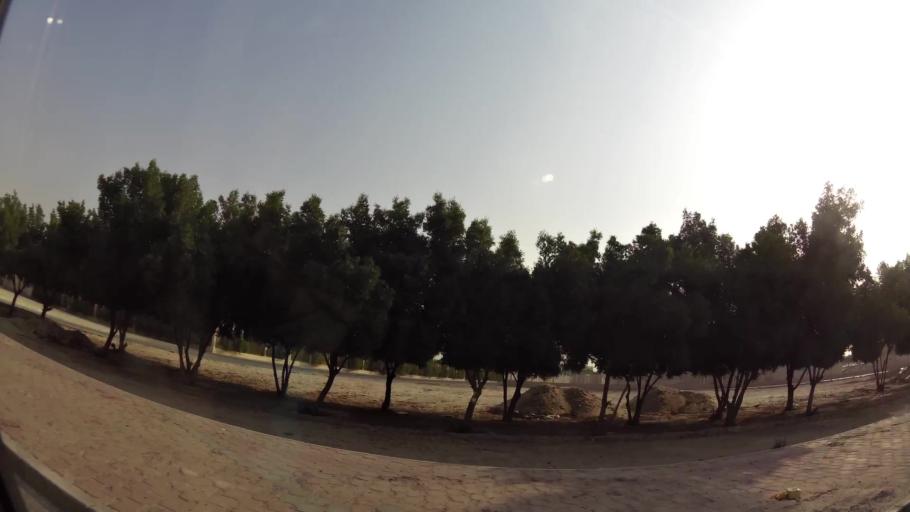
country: KW
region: Al Asimah
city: Ar Rabiyah
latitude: 29.3175
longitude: 47.8052
